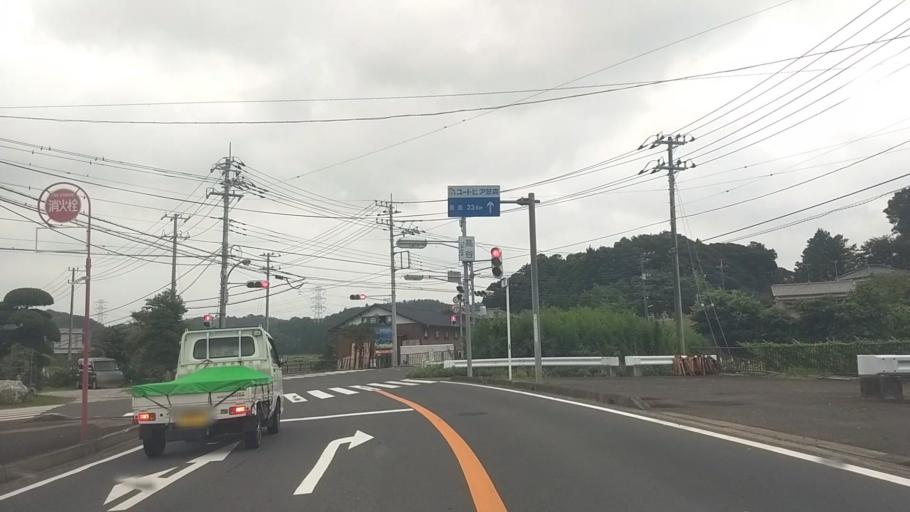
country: JP
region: Chiba
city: Ichihara
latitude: 35.3868
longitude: 140.0614
